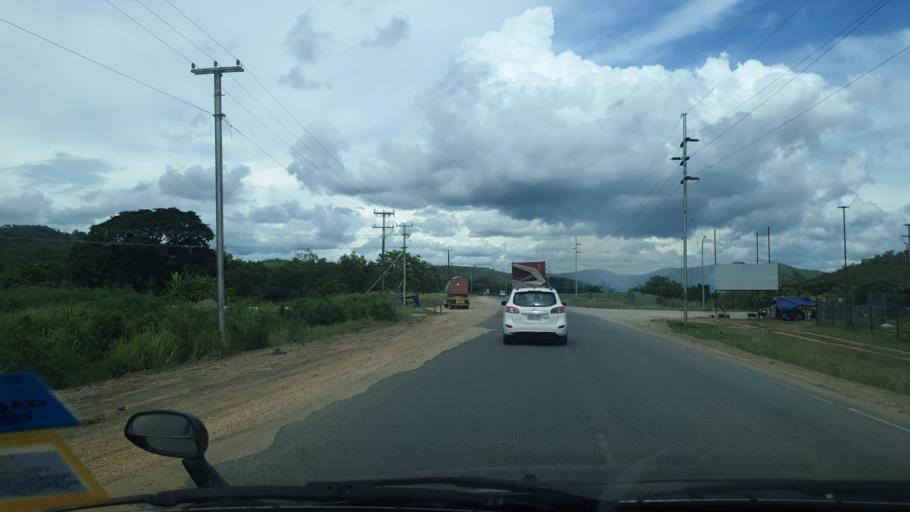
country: PG
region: National Capital
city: Port Moresby
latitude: -9.4163
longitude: 147.1112
